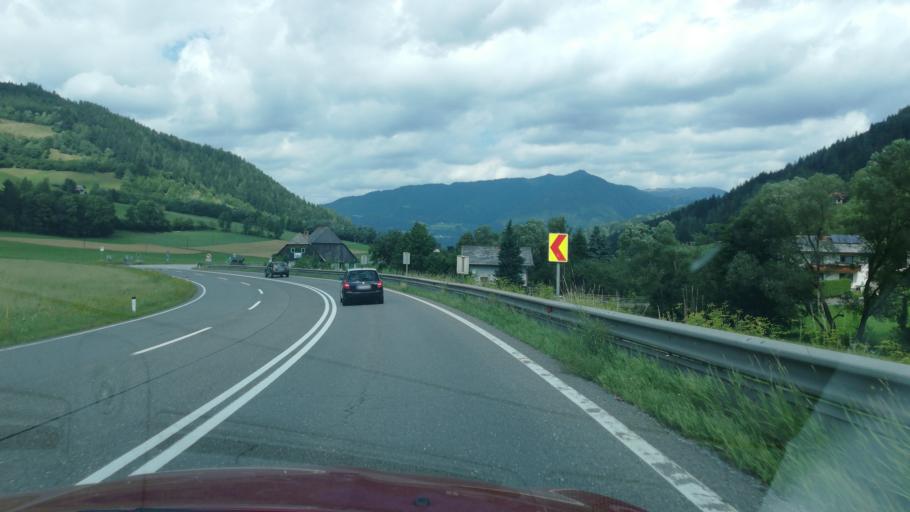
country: AT
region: Styria
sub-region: Politischer Bezirk Murau
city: Perchau am Sattel
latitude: 47.1260
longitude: 14.4415
